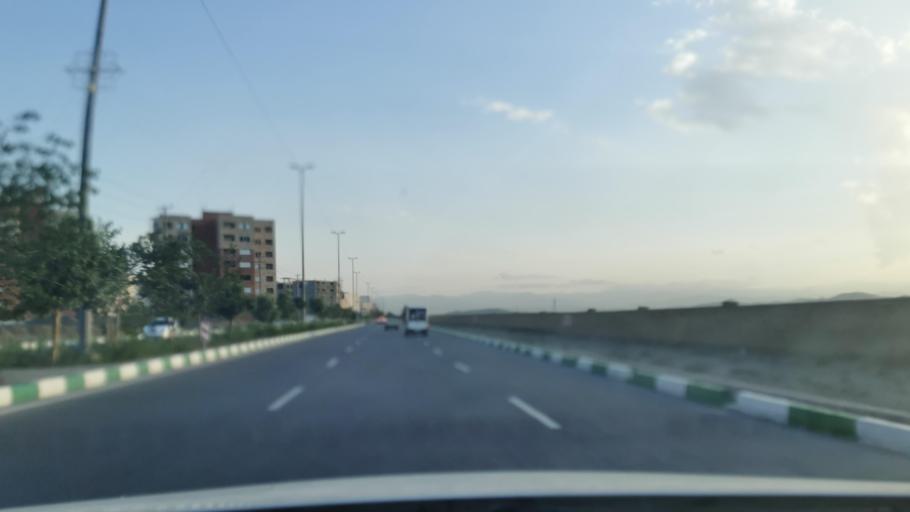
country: IR
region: Razavi Khorasan
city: Mashhad
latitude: 36.3949
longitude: 59.4738
